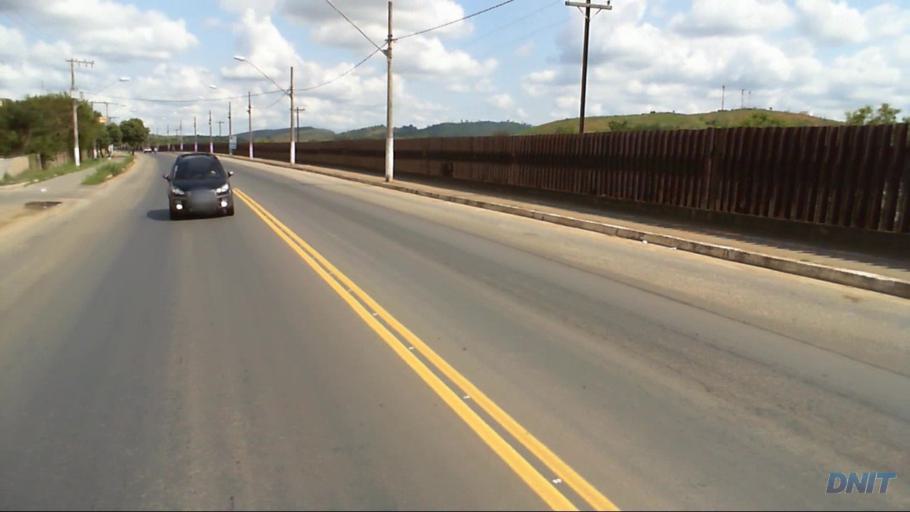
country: BR
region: Minas Gerais
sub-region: Governador Valadares
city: Governador Valadares
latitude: -18.8918
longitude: -41.9769
